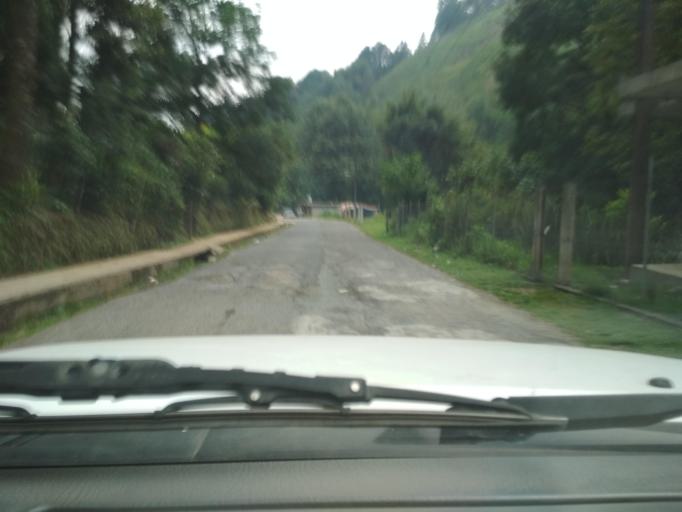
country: MX
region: Veracruz
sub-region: La Perla
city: Barrio de San Miguel
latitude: 18.9384
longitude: -97.1278
